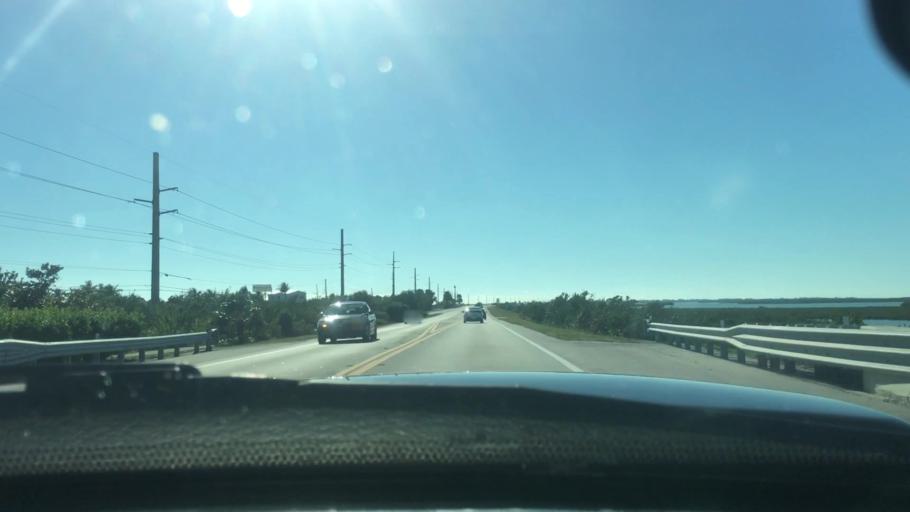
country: US
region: Florida
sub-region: Monroe County
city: Big Coppitt Key
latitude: 24.6266
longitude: -81.5978
